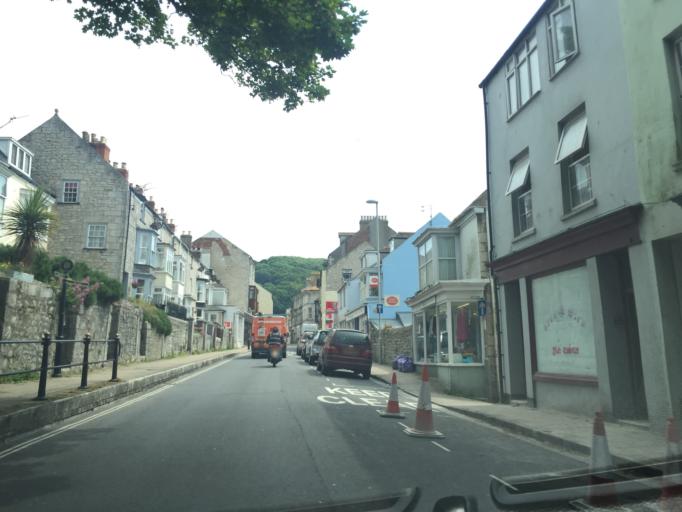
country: GB
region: England
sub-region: Dorset
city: Fortuneswell
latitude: 50.5606
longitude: -2.4440
